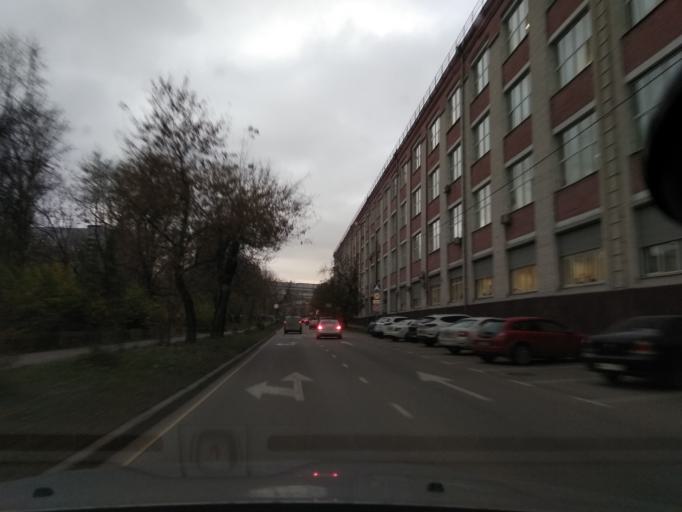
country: RU
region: Moscow
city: Mar'ina Roshcha
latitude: 55.7982
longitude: 37.6061
